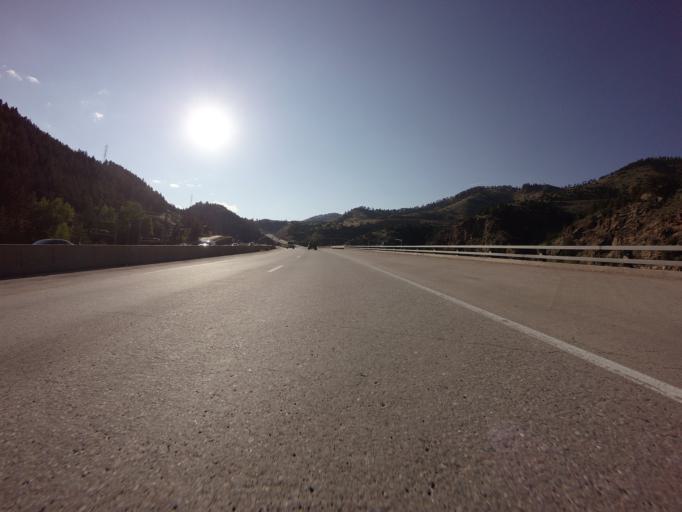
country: US
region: Colorado
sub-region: Clear Creek County
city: Idaho Springs
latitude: 39.7462
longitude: -105.4597
